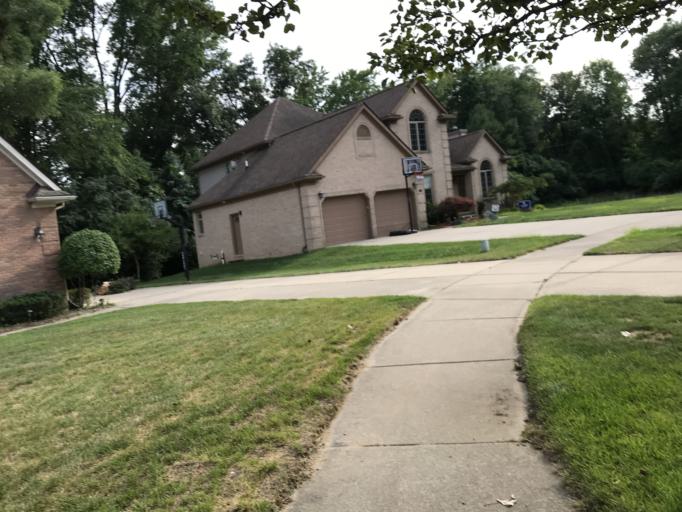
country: US
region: Michigan
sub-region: Oakland County
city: Franklin
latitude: 42.4966
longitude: -83.3327
